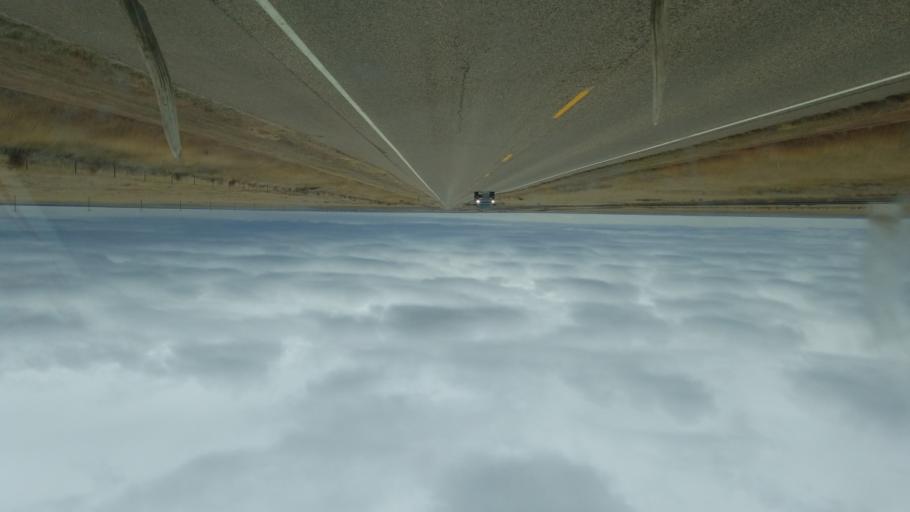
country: US
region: Colorado
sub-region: Kiowa County
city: Eads
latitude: 38.7663
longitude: -102.7730
